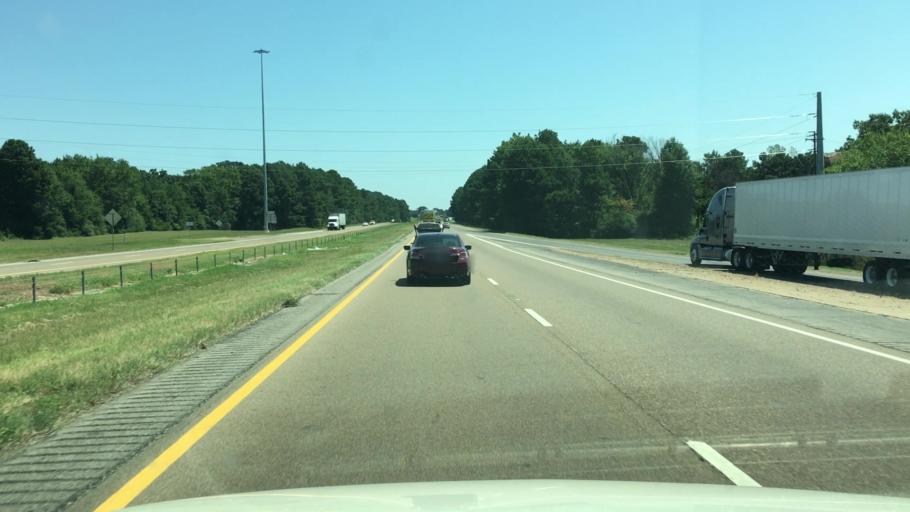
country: US
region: Texas
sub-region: Bowie County
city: New Boston
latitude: 33.4719
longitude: -94.4543
